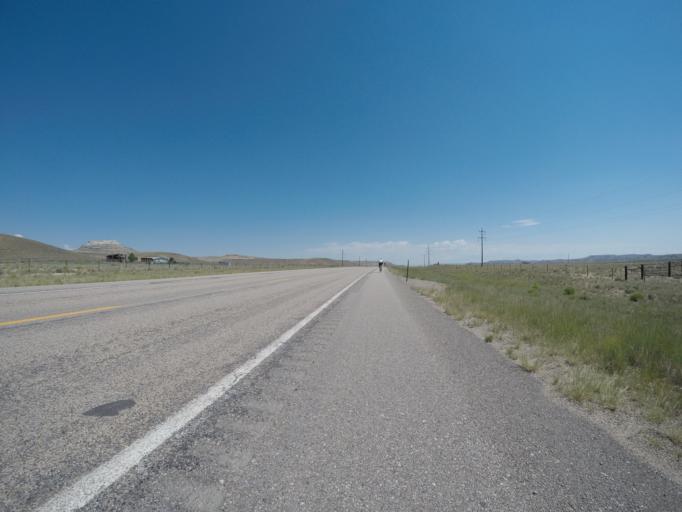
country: US
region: Wyoming
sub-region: Sublette County
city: Marbleton
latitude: 42.3702
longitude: -110.1492
